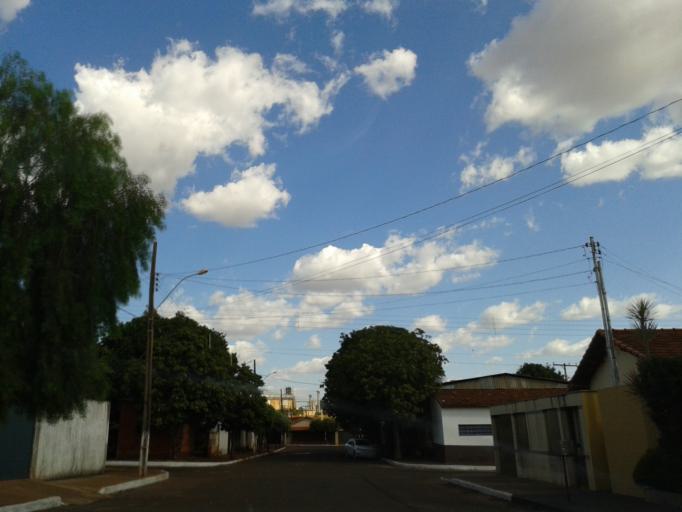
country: BR
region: Minas Gerais
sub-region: Capinopolis
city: Capinopolis
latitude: -18.6894
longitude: -49.5685
